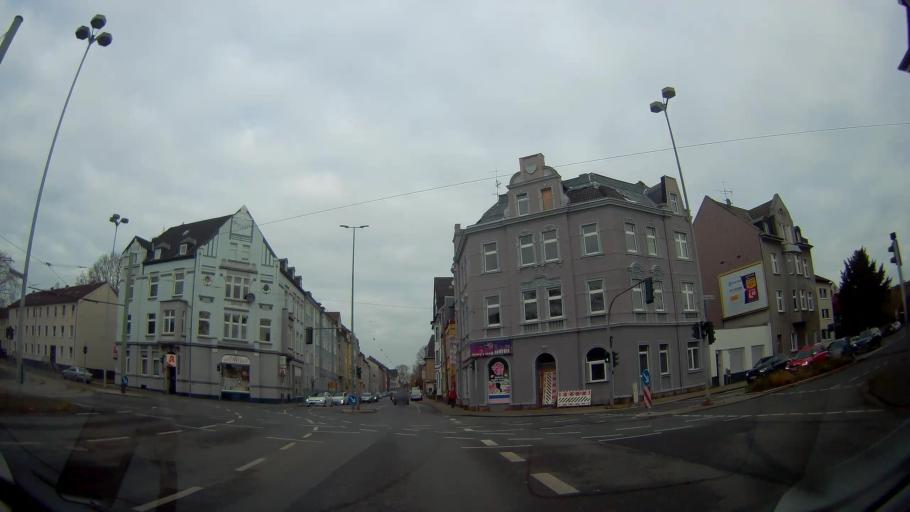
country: DE
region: North Rhine-Westphalia
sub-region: Regierungsbezirk Munster
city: Gelsenkirchen
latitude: 51.4934
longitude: 7.1228
